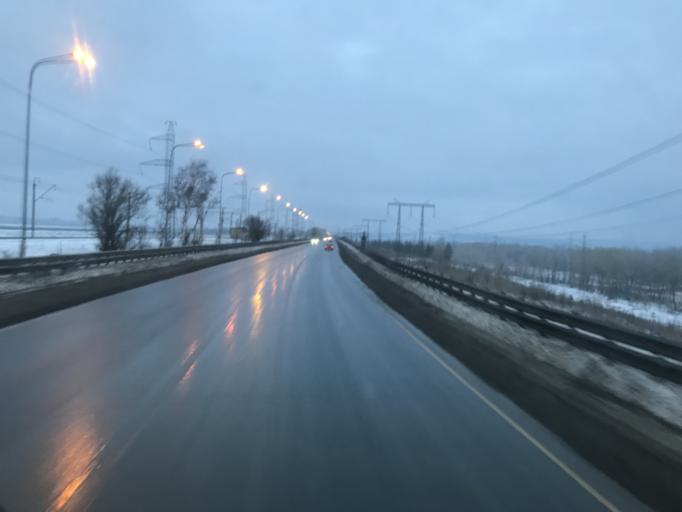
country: RU
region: Samara
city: Zhigulevsk
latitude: 53.4399
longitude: 49.4802
